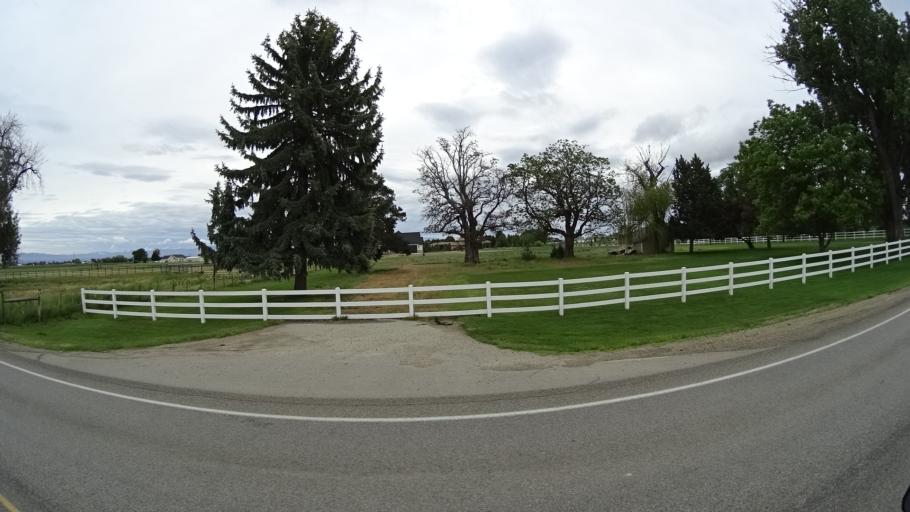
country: US
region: Idaho
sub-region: Ada County
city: Star
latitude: 43.6532
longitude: -116.4945
